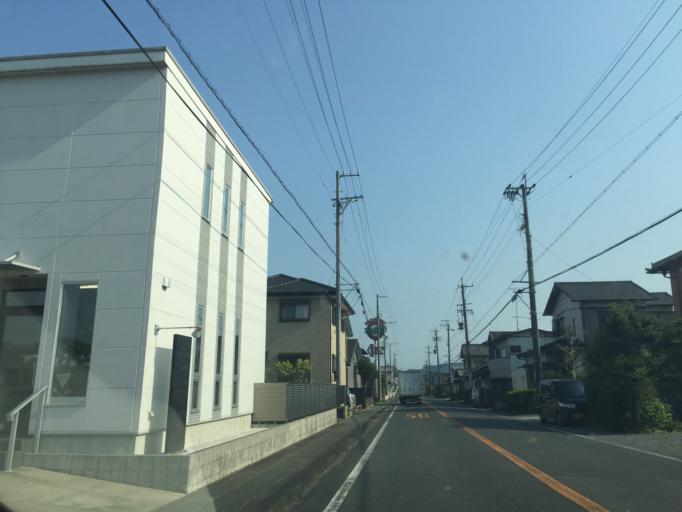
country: JP
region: Shizuoka
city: Kakegawa
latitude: 34.7956
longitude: 138.0127
